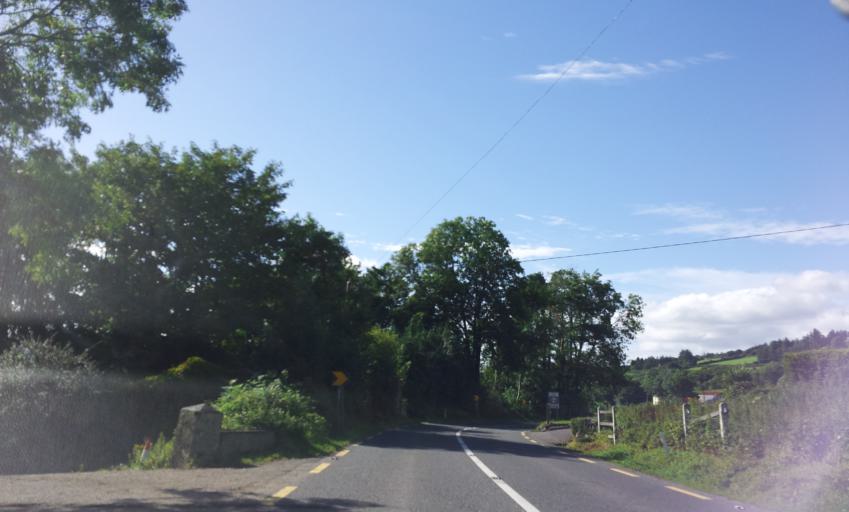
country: IE
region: Munster
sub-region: County Cork
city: Macroom
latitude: 51.9223
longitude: -9.0949
